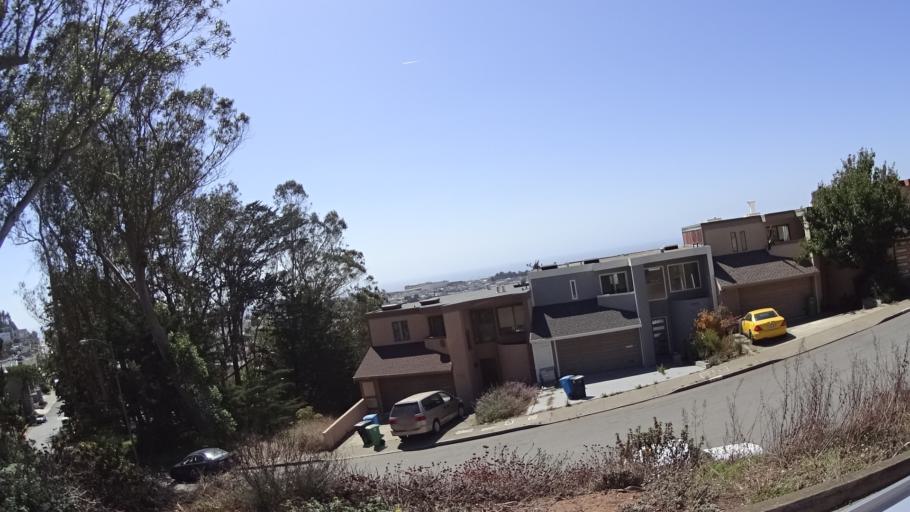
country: US
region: California
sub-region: San Mateo County
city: Daly City
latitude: 37.7557
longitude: -122.4722
